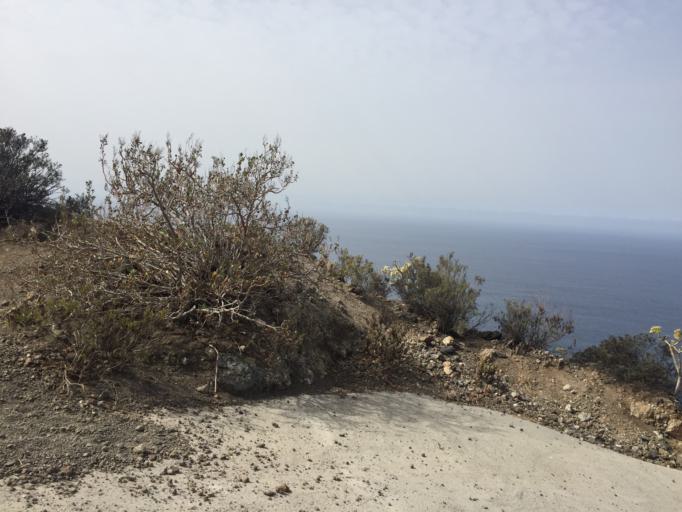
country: ES
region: Canary Islands
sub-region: Provincia de Santa Cruz de Tenerife
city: Tijarafe
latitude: 28.7171
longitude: -17.9786
